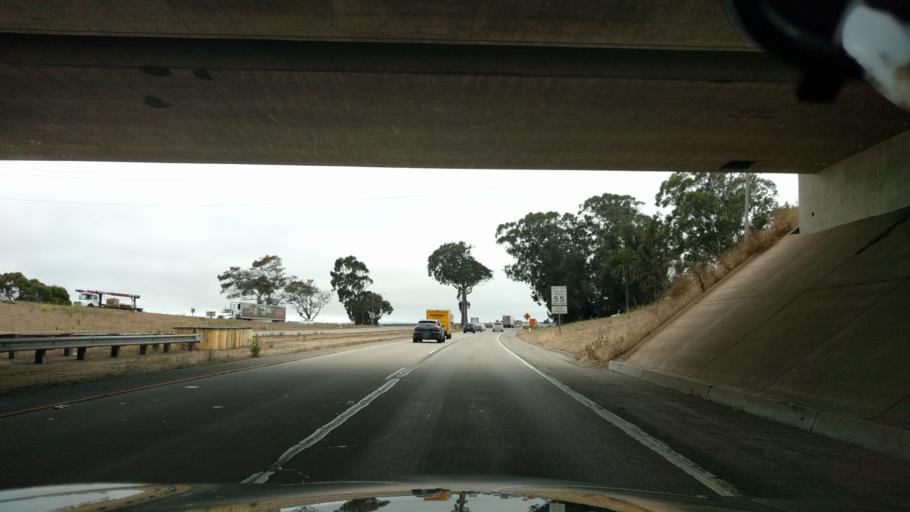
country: US
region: California
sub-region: Monterey County
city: Castroville
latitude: 36.7616
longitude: -121.7522
